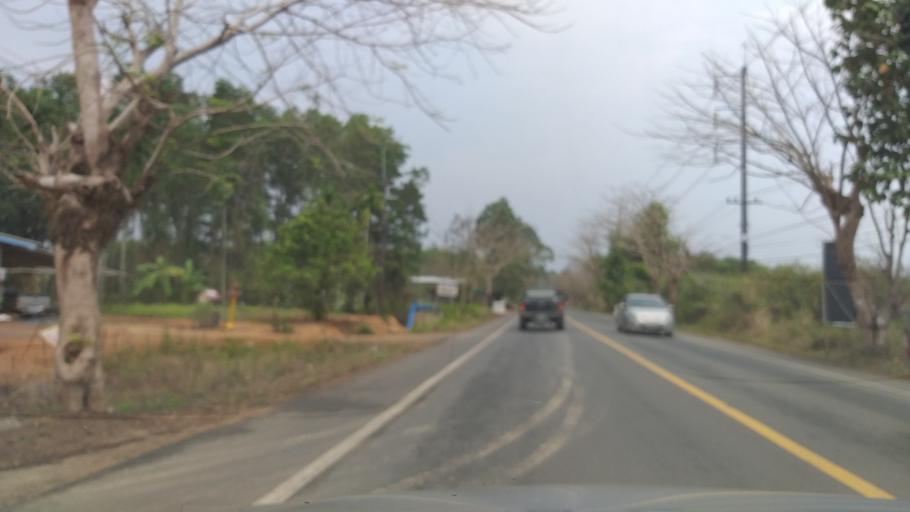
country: TH
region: Trat
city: Khao Saming
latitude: 12.3148
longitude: 102.3549
